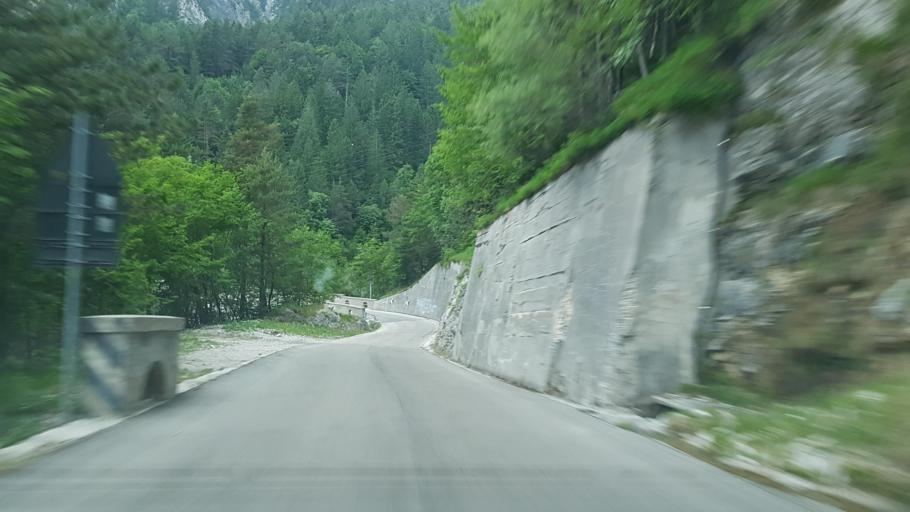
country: IT
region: Friuli Venezia Giulia
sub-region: Provincia di Udine
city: Pontebba
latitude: 46.5269
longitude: 13.3009
